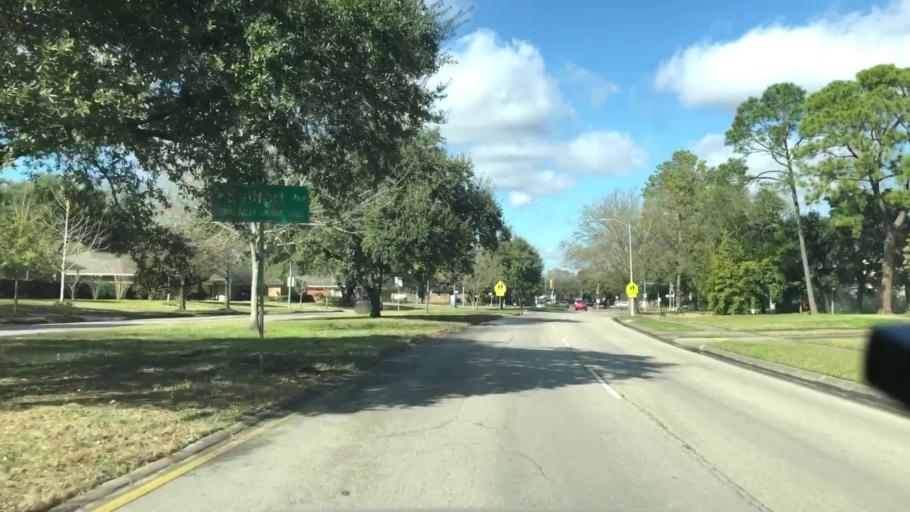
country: US
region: Texas
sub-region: Harris County
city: Bellaire
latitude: 29.6650
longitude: -95.4679
